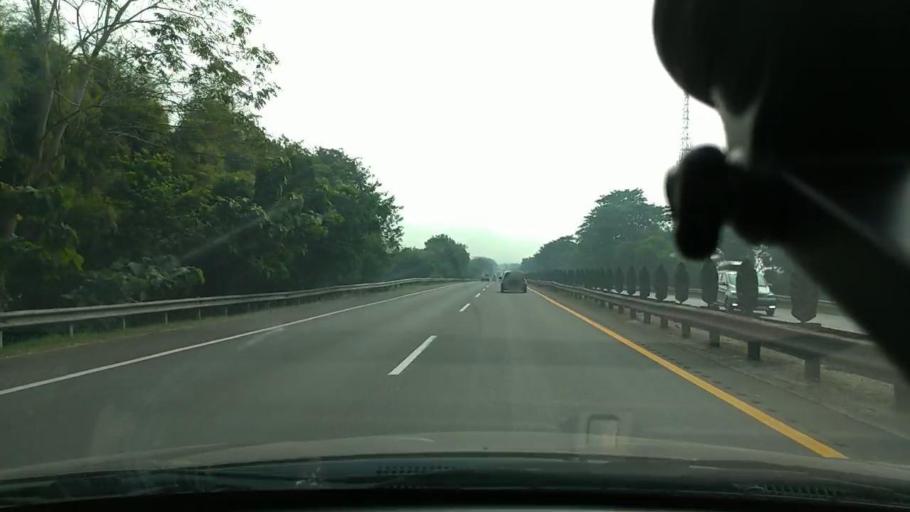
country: ID
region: Banten
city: Serang
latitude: -6.0921
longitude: 106.1559
